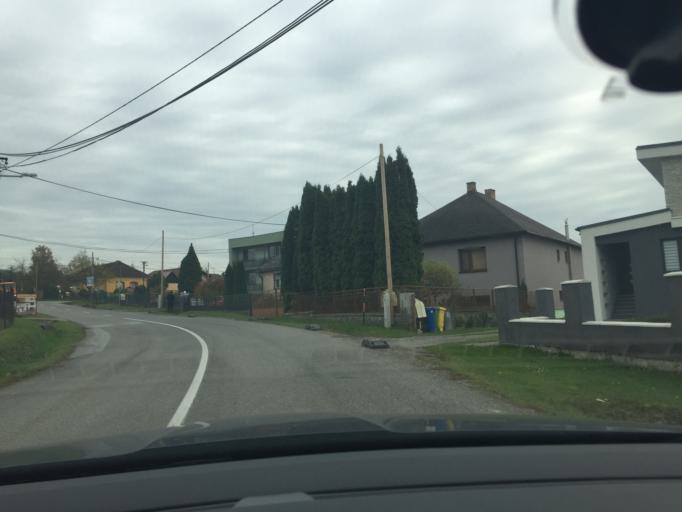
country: SK
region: Presovsky
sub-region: Okres Presov
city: Presov
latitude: 48.9478
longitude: 21.2865
